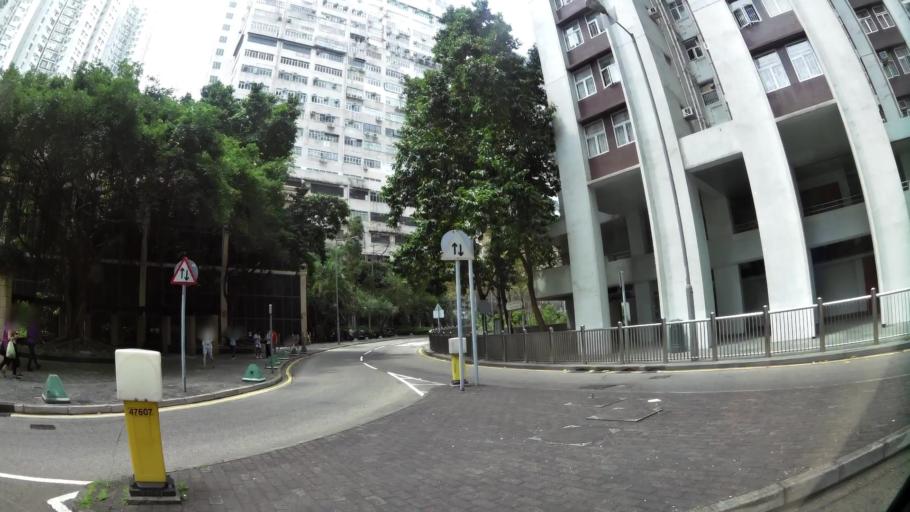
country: HK
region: Wanchai
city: Wan Chai
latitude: 22.2860
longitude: 114.2153
